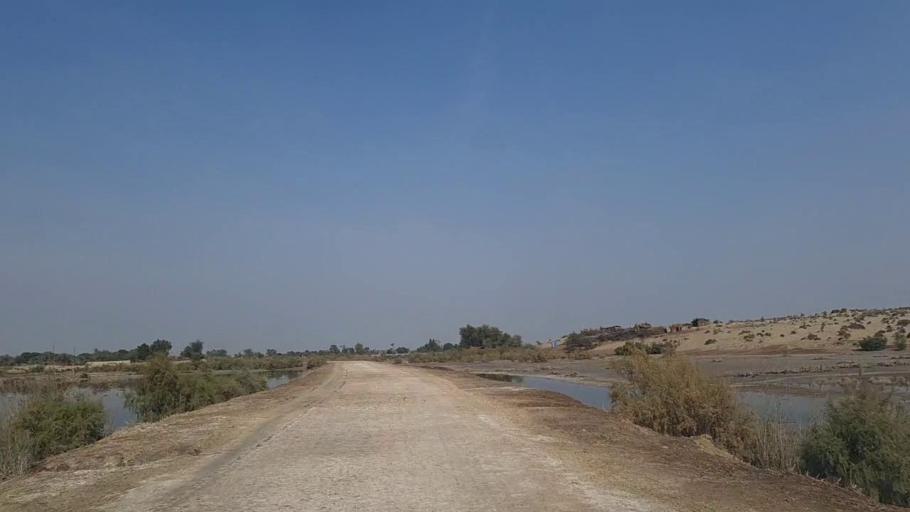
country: PK
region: Sindh
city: Daur
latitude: 26.5116
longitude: 68.4805
